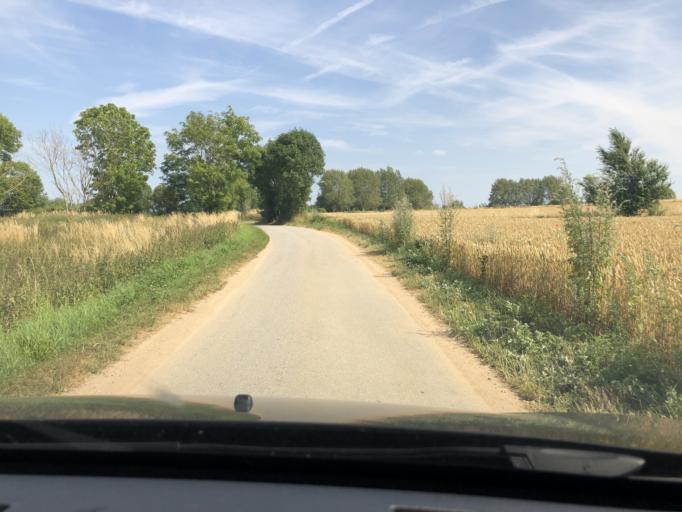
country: DK
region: South Denmark
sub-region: AEro Kommune
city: AEroskobing
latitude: 54.9137
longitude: 10.3044
